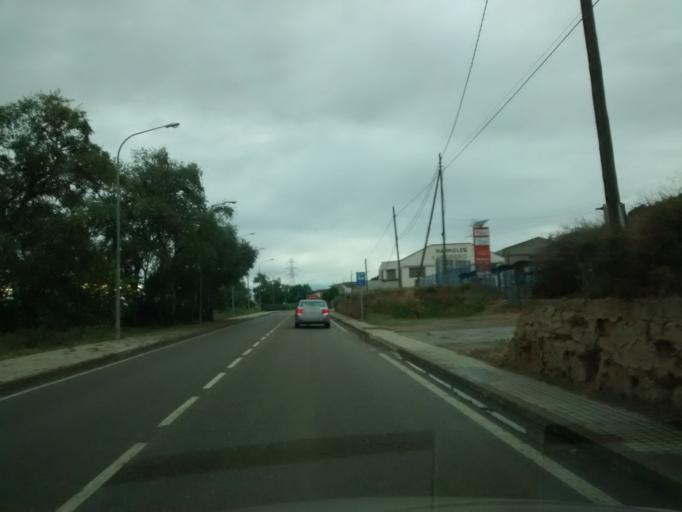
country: ES
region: Aragon
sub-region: Provincia de Zaragoza
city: Caspe
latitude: 41.2263
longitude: -0.0313
